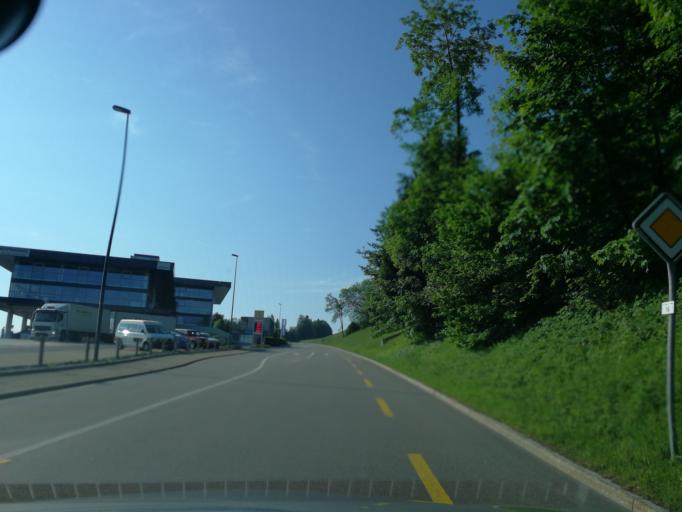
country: CH
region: Zurich
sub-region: Bezirk Horgen
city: Horgen / Allmend
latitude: 47.2382
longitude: 8.6110
